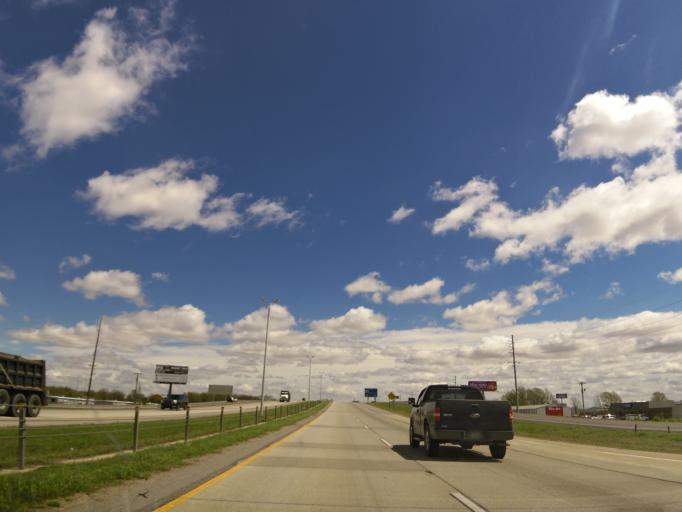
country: US
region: Arkansas
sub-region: Craighead County
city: Jonesboro
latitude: 35.8070
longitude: -90.6620
